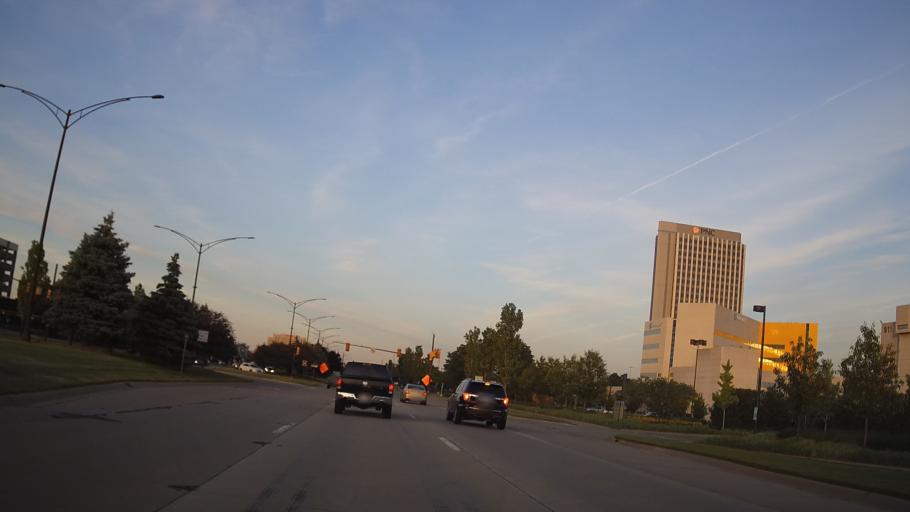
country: US
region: Michigan
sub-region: Oakland County
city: Clawson
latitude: 42.5618
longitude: -83.1662
